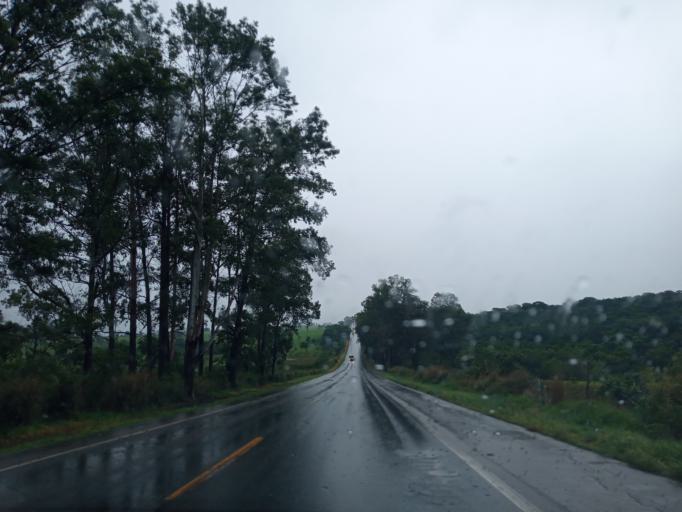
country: BR
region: Minas Gerais
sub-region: Luz
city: Luz
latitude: -19.7838
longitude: -45.7003
